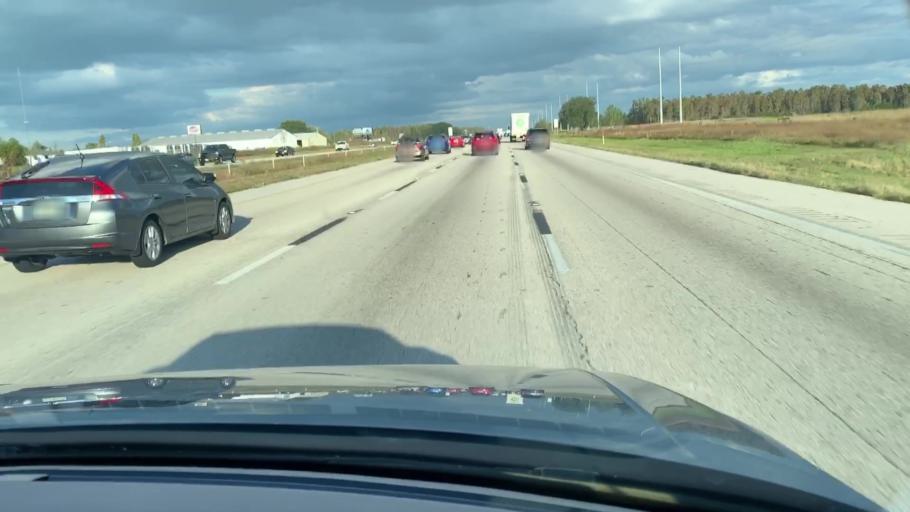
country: US
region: Florida
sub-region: Polk County
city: Polk City
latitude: 28.1415
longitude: -81.8904
